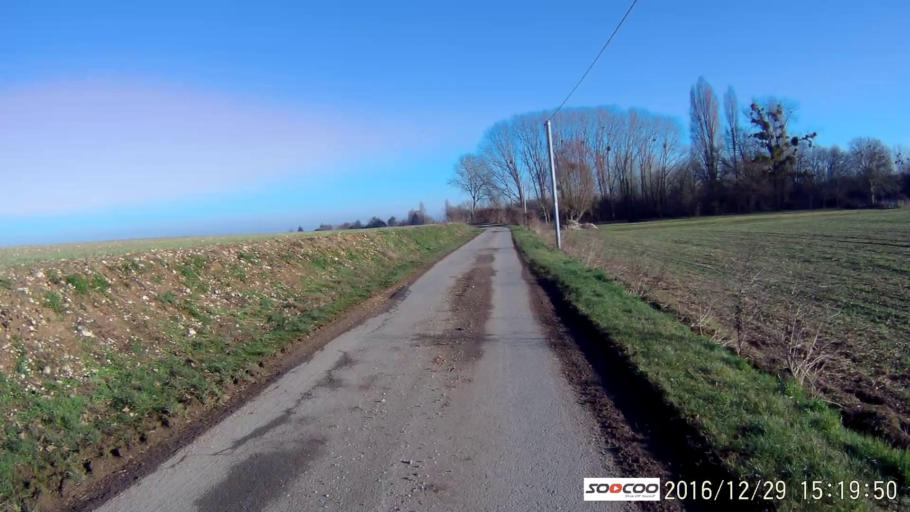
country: FR
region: Centre
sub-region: Departement de l'Indre
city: Neuvy-Pailloux
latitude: 46.9376
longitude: 1.8057
